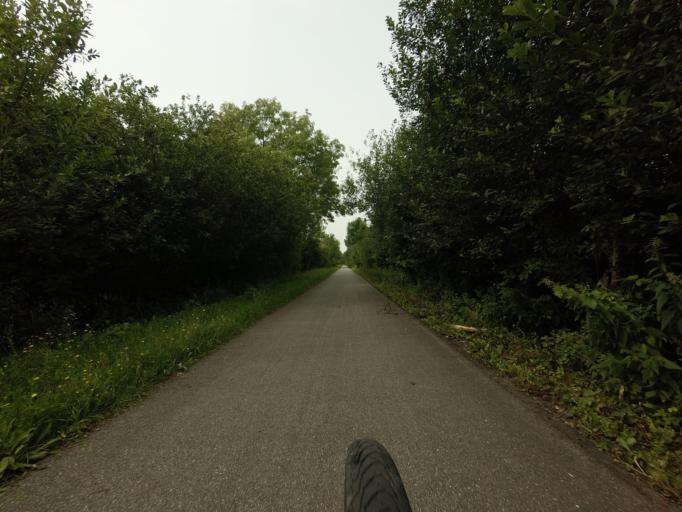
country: DK
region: Zealand
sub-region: Naestved Kommune
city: Fuglebjerg
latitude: 55.2608
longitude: 11.5817
